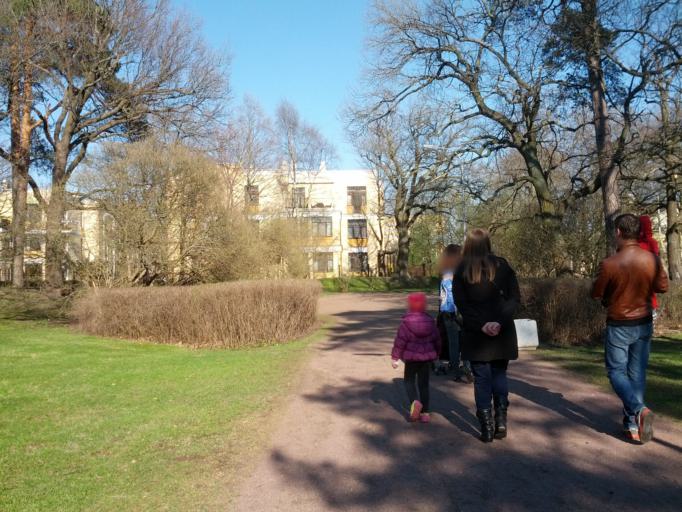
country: RU
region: St.-Petersburg
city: Sestroretsk
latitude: 60.0893
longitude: 29.9413
